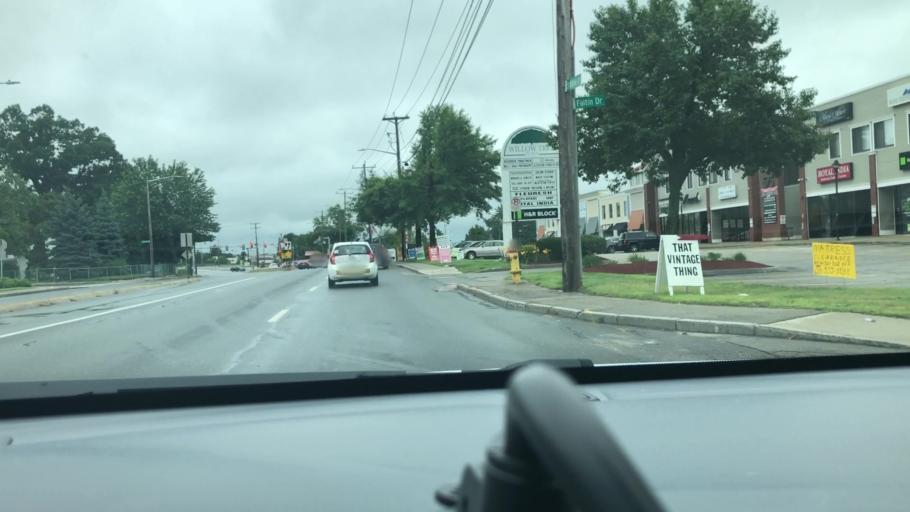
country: US
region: New Hampshire
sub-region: Hillsborough County
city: Manchester
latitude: 42.9663
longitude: -71.4494
